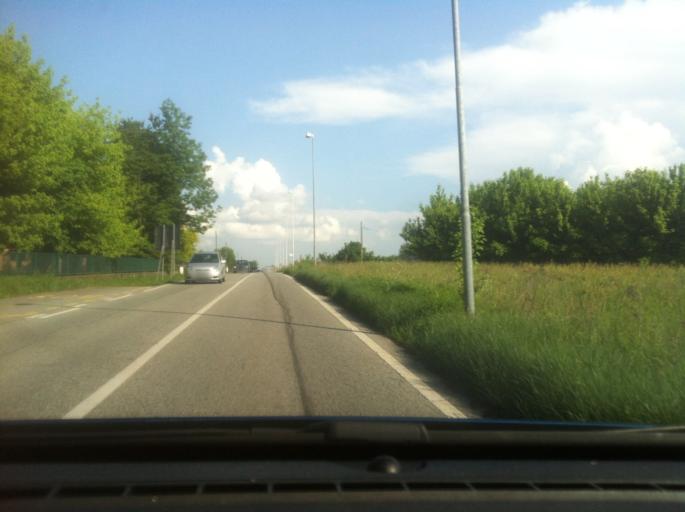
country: IT
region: Piedmont
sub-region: Provincia di Torino
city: Pavone Canavese
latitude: 45.4337
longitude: 7.8509
